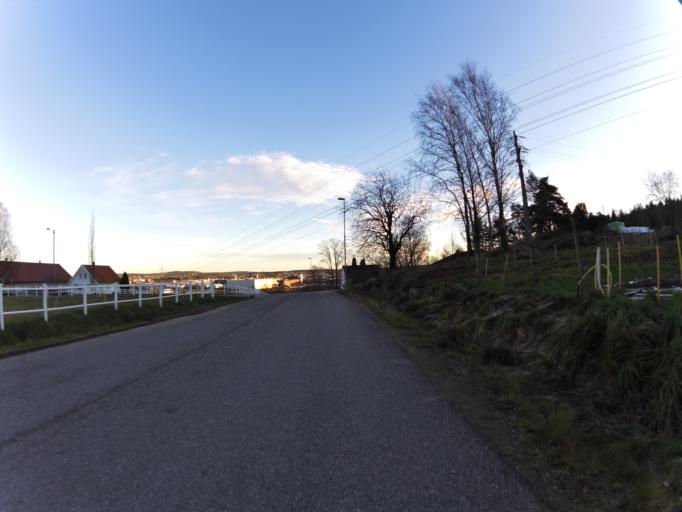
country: NO
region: Ostfold
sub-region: Fredrikstad
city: Fredrikstad
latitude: 59.2443
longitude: 10.9669
